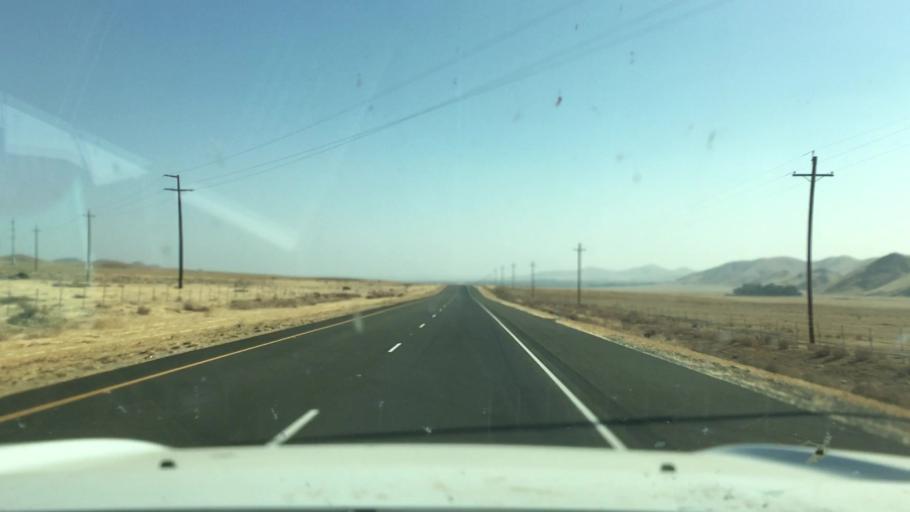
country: US
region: California
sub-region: San Luis Obispo County
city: Shandon
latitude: 35.7085
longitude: -120.1607
